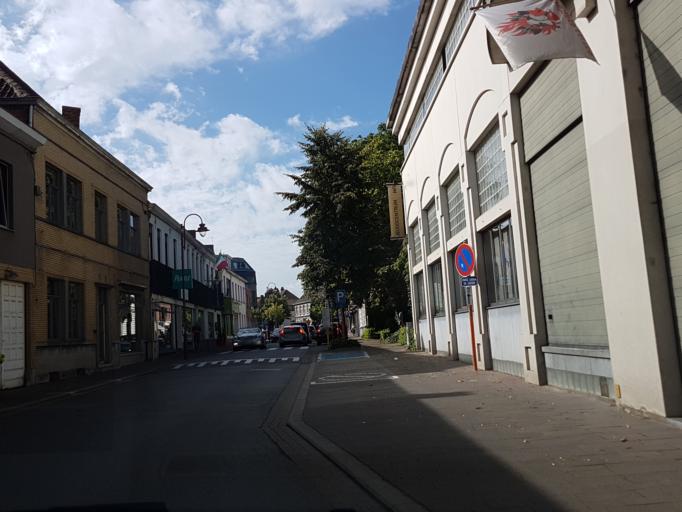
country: BE
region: Flanders
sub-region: Provincie Oost-Vlaanderen
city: Aalter
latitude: 51.0867
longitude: 3.4483
